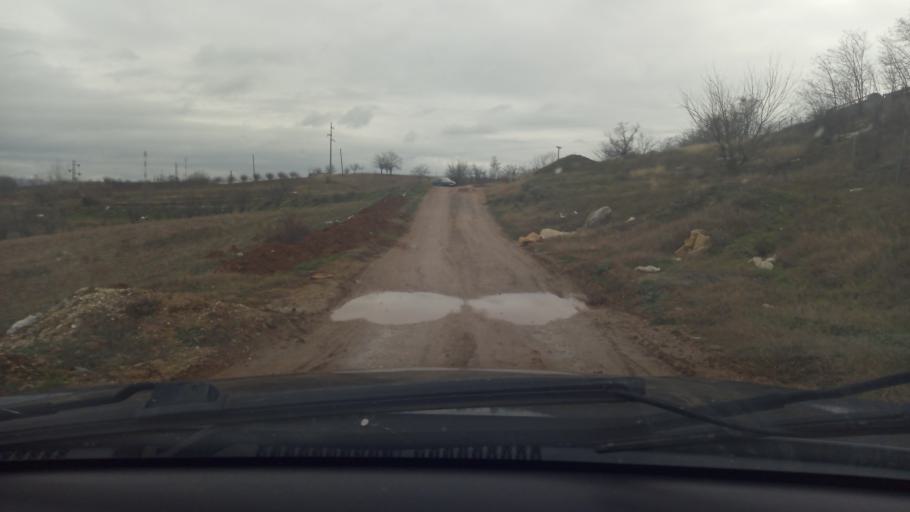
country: MK
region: Gradsko
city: Gradsko
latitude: 41.5738
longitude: 21.9363
